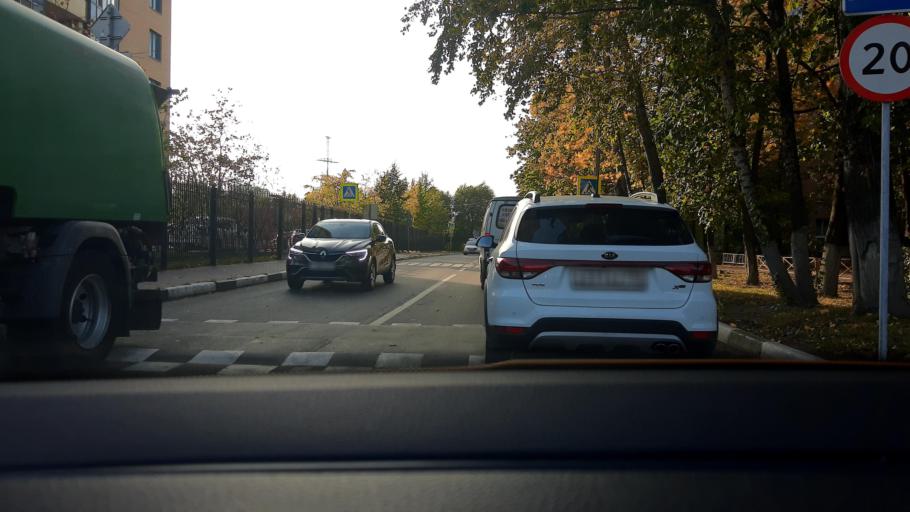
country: RU
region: Moskovskaya
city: Reutov
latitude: 55.7608
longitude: 37.8484
